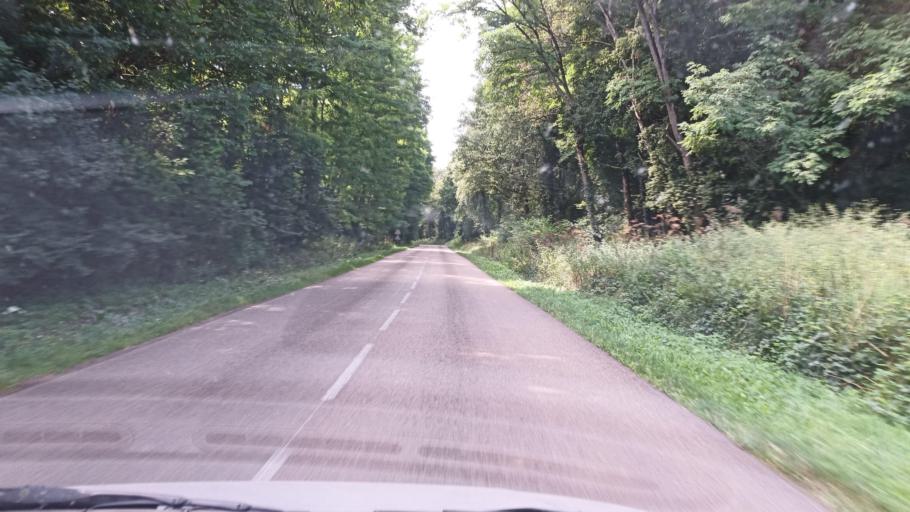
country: FR
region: Bourgogne
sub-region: Departement de l'Yonne
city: Villeneuve-sur-Yonne
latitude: 48.0758
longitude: 3.2690
